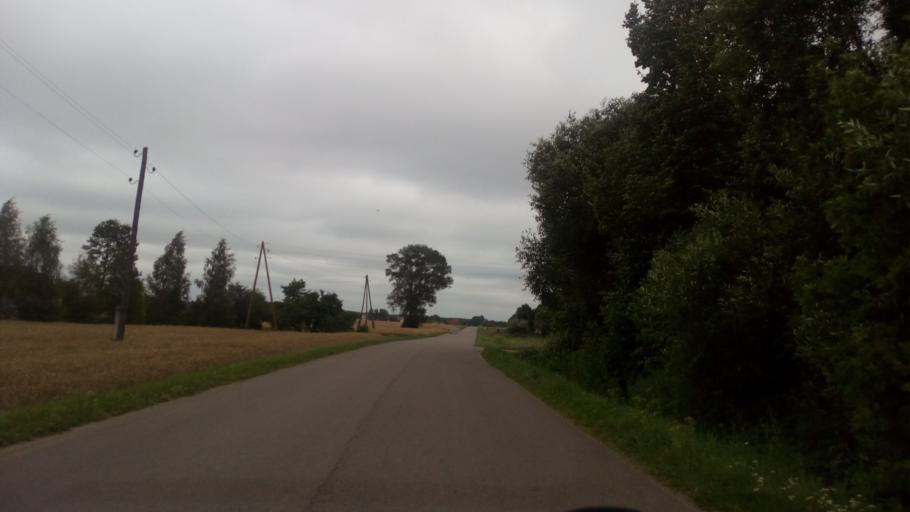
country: LV
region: Rundales
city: Pilsrundale
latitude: 56.4258
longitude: 23.9888
